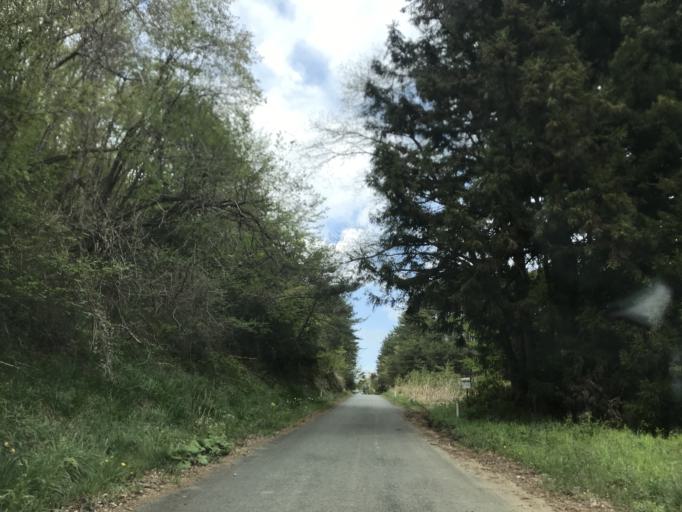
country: JP
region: Iwate
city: Ichinoseki
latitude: 38.7867
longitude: 141.4344
